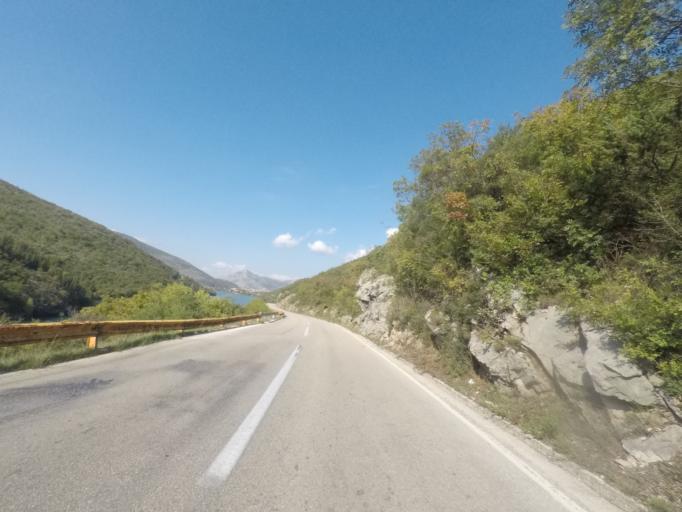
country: BA
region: Republika Srpska
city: Trebinje
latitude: 42.7033
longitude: 18.4172
